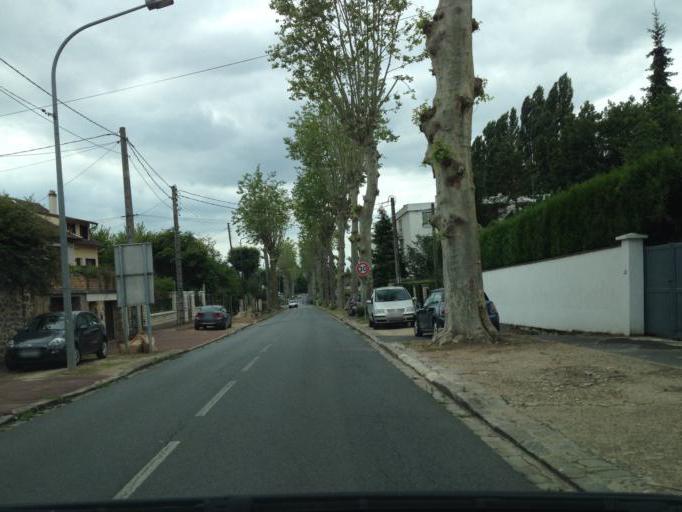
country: FR
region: Ile-de-France
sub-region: Departement de l'Essonne
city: Gif-sur-Yvette
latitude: 48.6973
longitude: 2.1492
